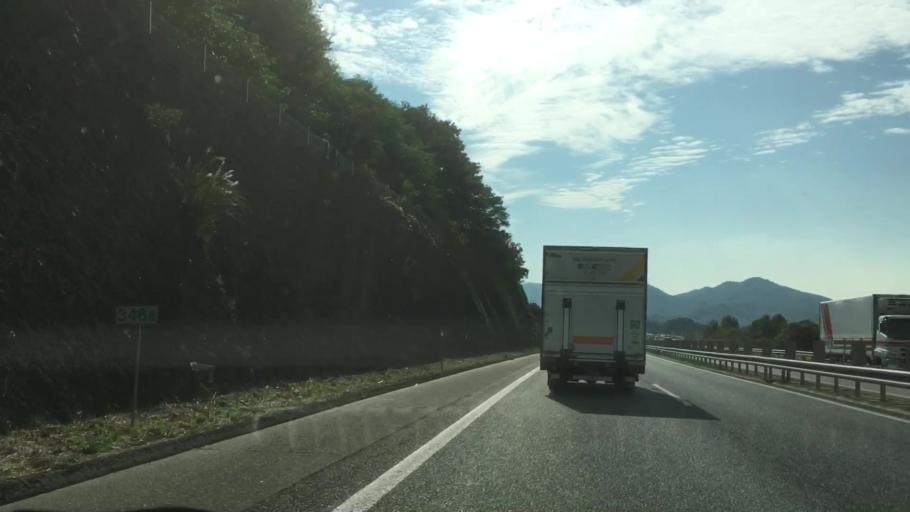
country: JP
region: Yamaguchi
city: Yanai
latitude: 34.0843
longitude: 132.0855
